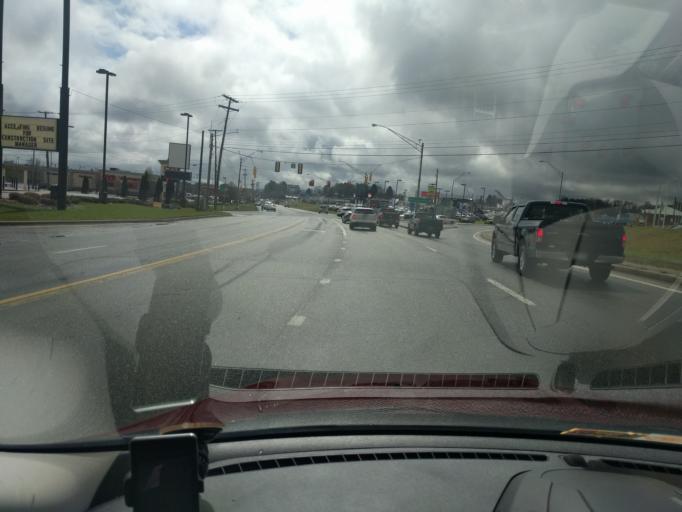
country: US
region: West Virginia
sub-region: Raleigh County
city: Beckley
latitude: 37.8065
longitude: -81.1848
